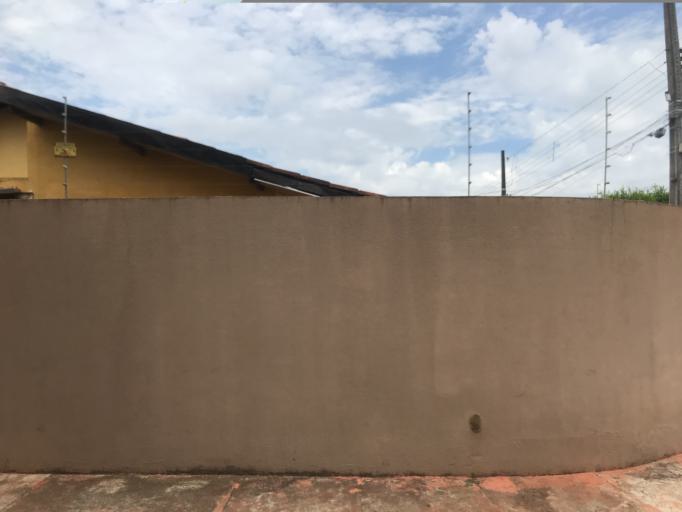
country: BR
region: Parana
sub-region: Londrina
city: Londrina
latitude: -23.2893
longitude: -51.2071
